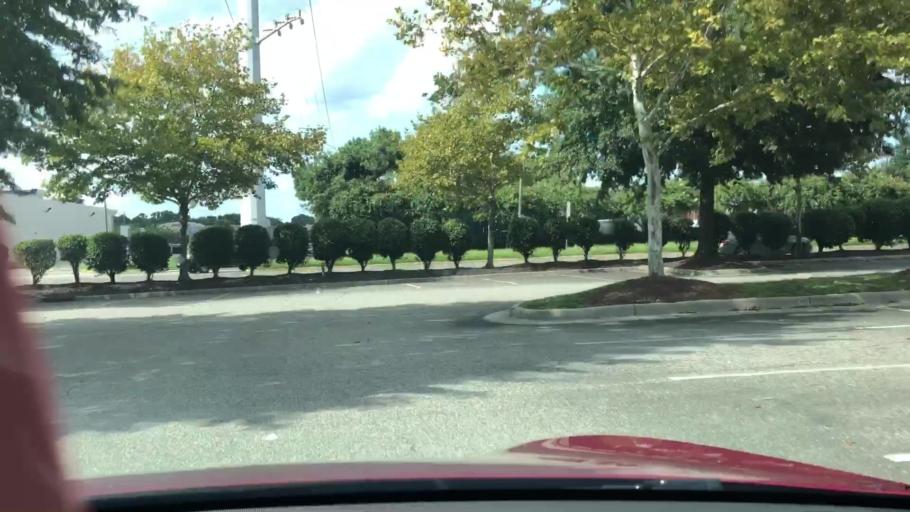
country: US
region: Virginia
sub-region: City of Virginia Beach
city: Virginia Beach
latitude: 36.8478
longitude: -76.0233
